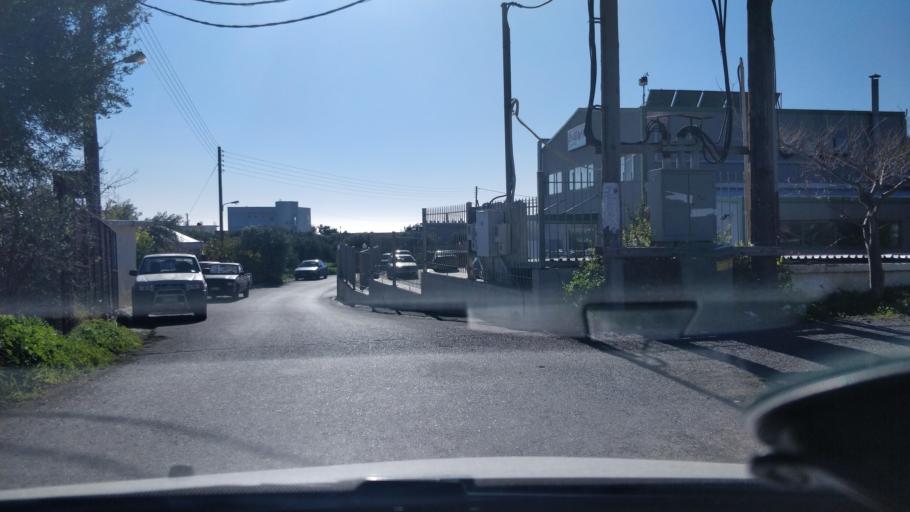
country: GR
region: Crete
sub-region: Nomos Lasithiou
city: Gra Liyia
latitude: 35.0153
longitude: 25.6767
